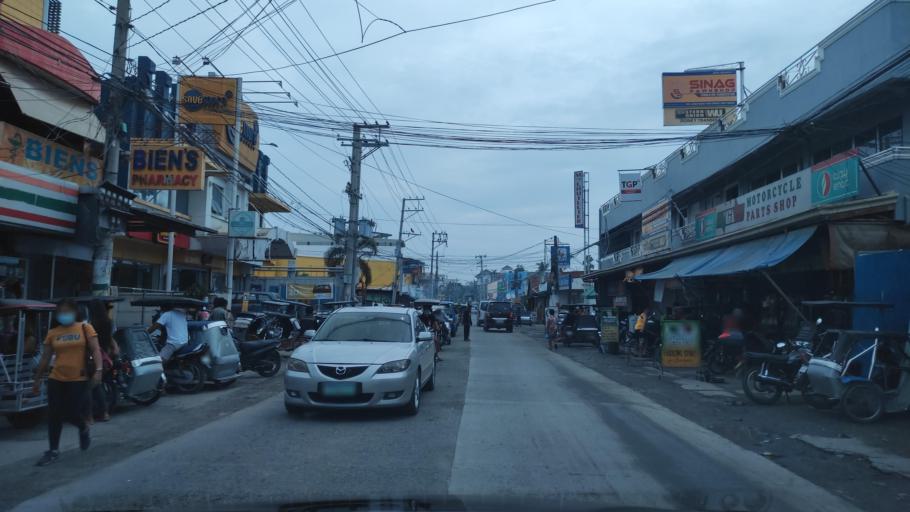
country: PH
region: Central Luzon
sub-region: Province of Nueva Ecija
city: San Anton
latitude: 15.3387
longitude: 120.9119
